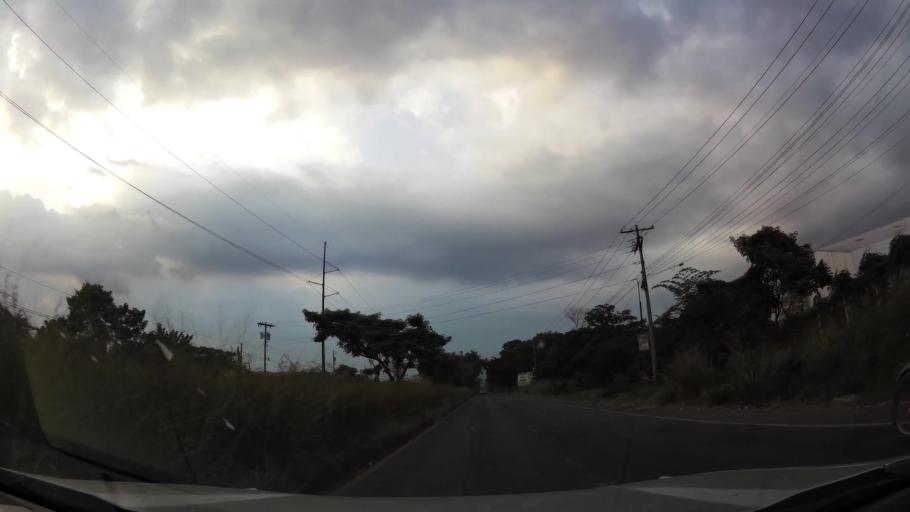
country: GT
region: Escuintla
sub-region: Municipio de Escuintla
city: Escuintla
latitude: 14.2768
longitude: -90.7782
